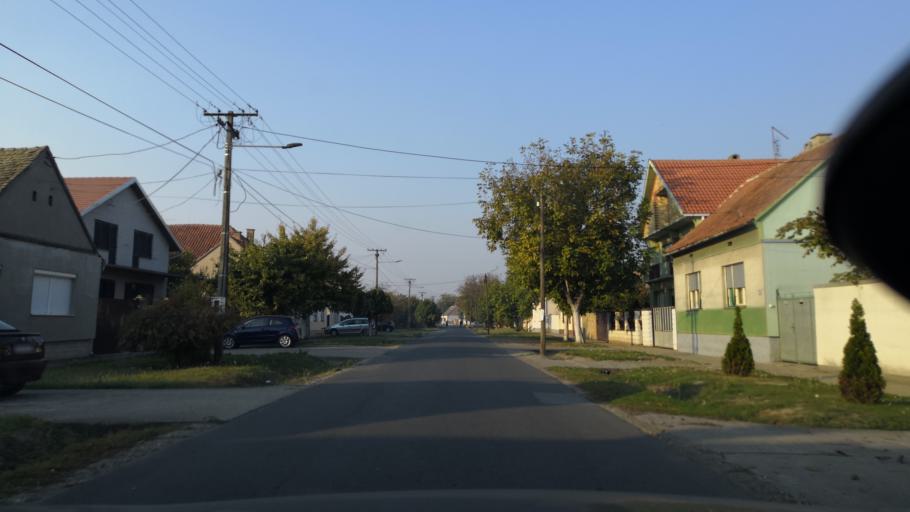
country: RS
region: Autonomna Pokrajina Vojvodina
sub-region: Sremski Okrug
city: Stara Pazova
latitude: 44.9885
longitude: 20.1497
